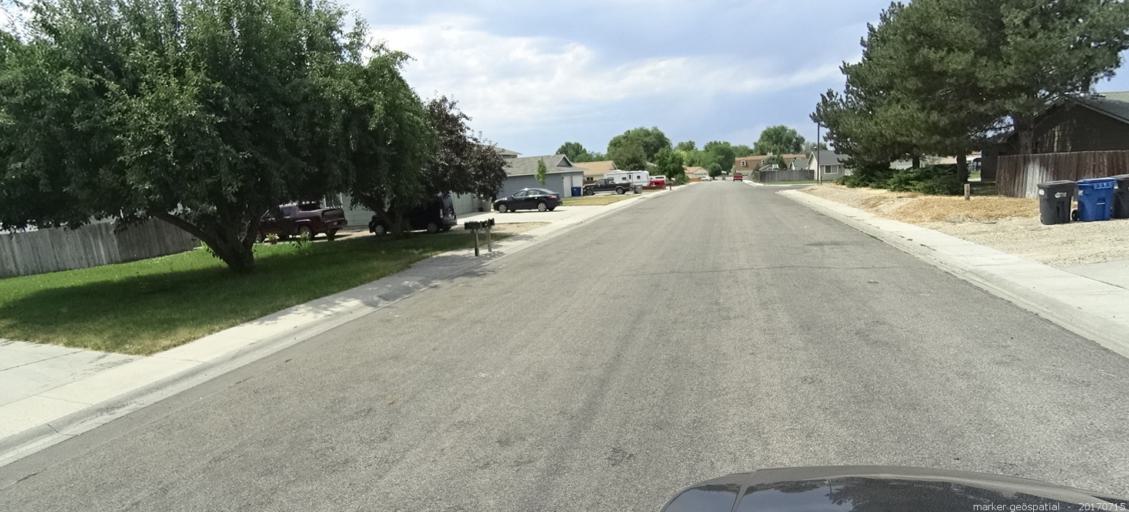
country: US
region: Idaho
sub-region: Ada County
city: Garden City
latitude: 43.5689
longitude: -116.3100
